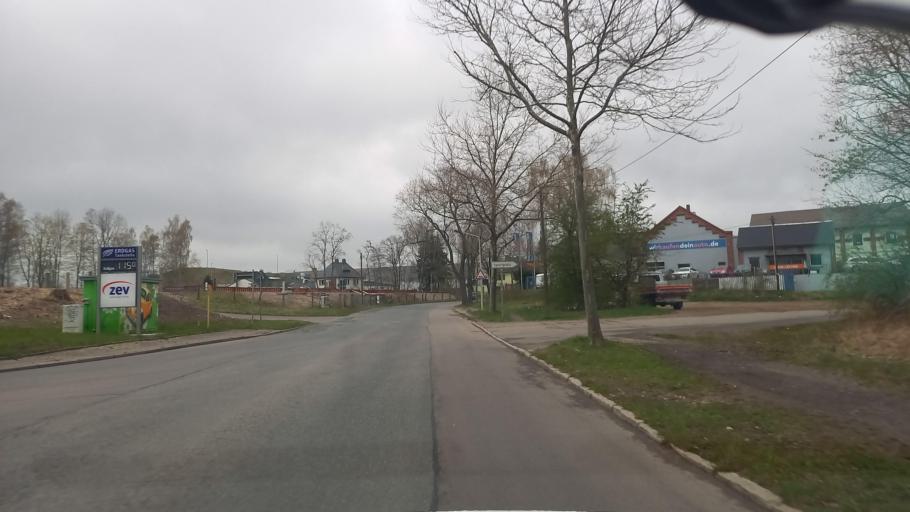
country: DE
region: Saxony
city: Zwickau
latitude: 50.7055
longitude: 12.4835
